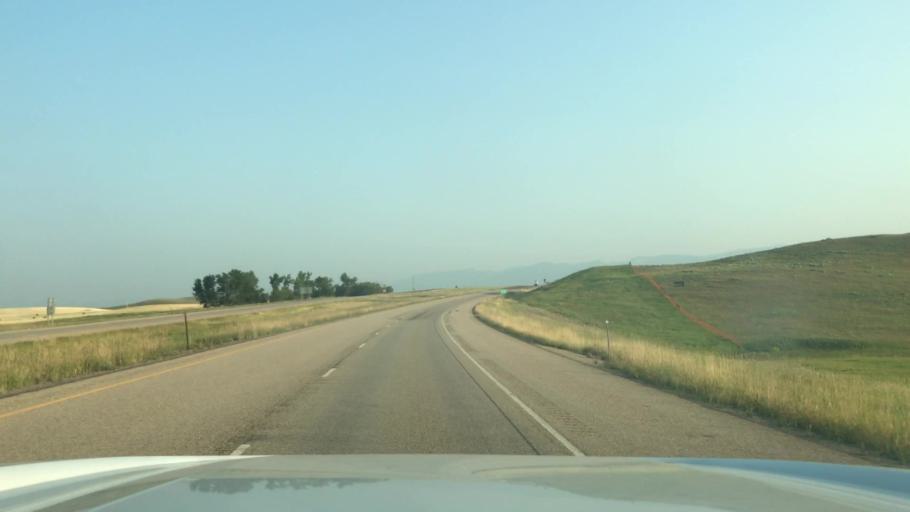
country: US
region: Wyoming
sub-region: Sheridan County
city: Sheridan
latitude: 45.0044
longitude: -107.2990
